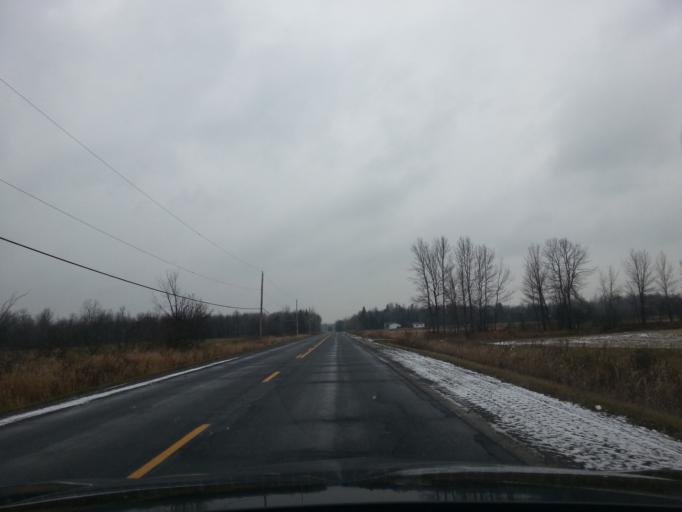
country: CA
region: Ontario
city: Carleton Place
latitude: 45.0872
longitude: -76.0134
